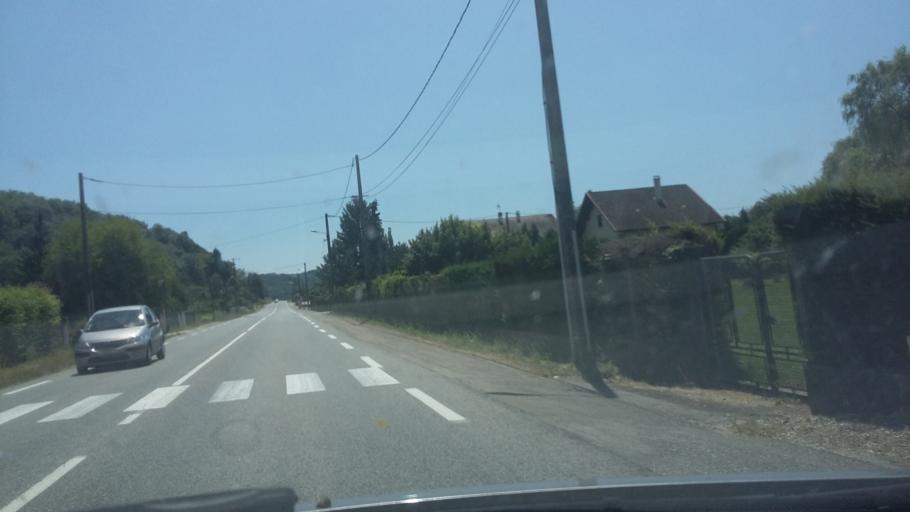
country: FR
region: Rhone-Alpes
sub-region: Departement de l'Ain
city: Belley
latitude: 45.7994
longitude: 5.6821
